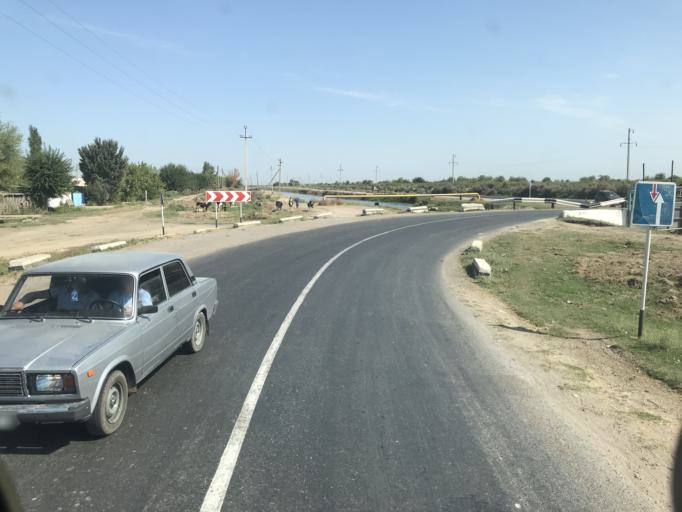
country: KZ
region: Ongtustik Qazaqstan
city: Myrzakent
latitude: 40.7161
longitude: 68.5338
